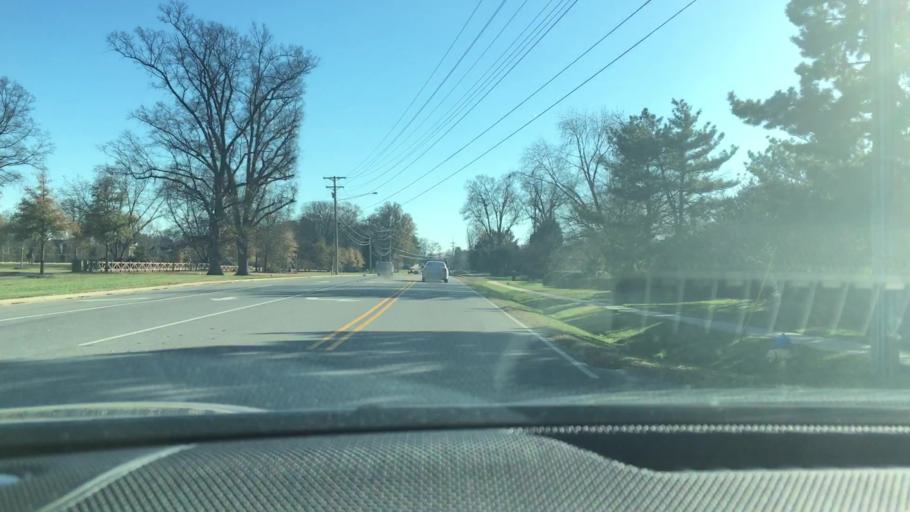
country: US
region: North Carolina
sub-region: Mecklenburg County
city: Cornelius
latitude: 35.4582
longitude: -80.8886
